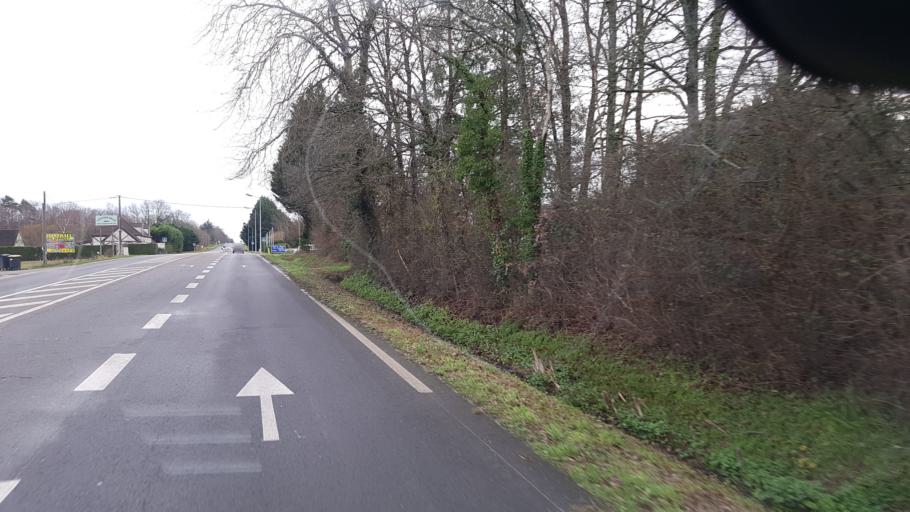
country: FR
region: Centre
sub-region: Departement du Loiret
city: Menestreau-en-Villette
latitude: 47.6531
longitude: 1.9871
